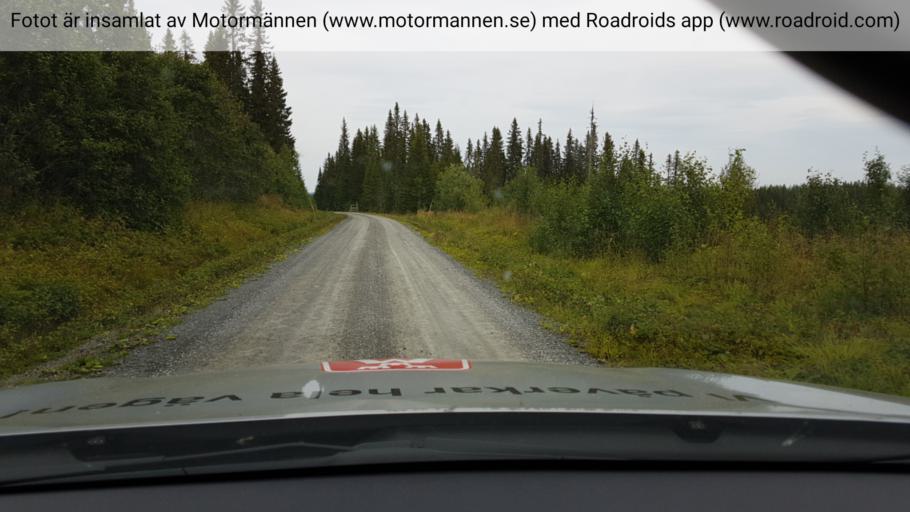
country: SE
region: Jaemtland
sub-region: Krokoms Kommun
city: Valla
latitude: 63.5780
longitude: 13.9427
